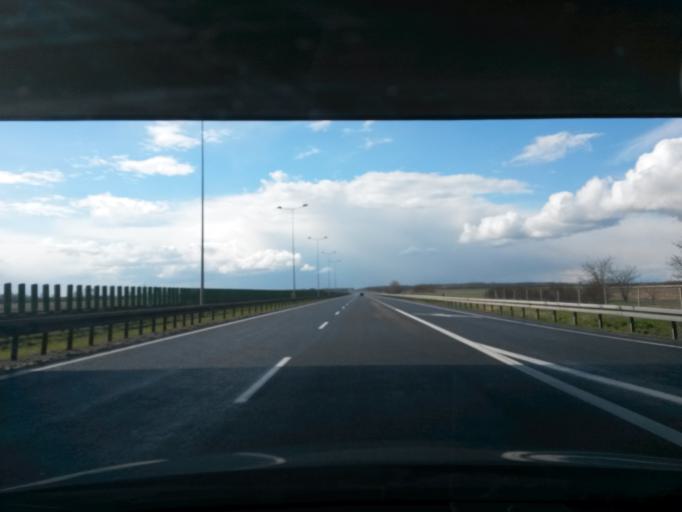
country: PL
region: Greater Poland Voivodeship
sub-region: Powiat wrzesinski
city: Kolaczkowo
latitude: 52.2950
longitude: 17.6505
